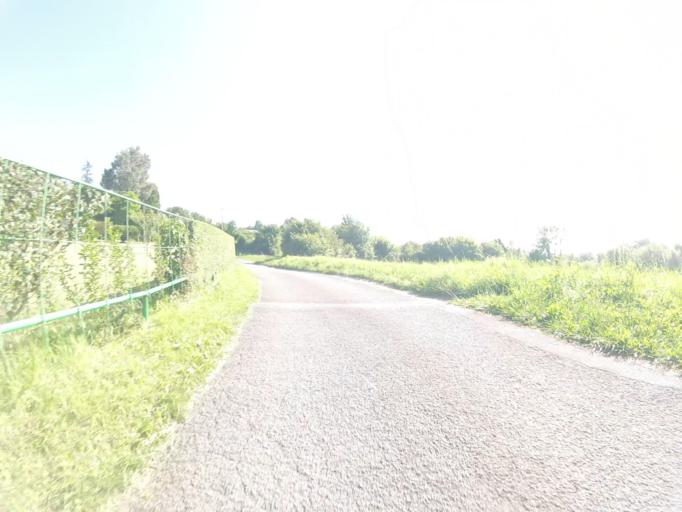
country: ES
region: Basque Country
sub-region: Provincia de Guipuzcoa
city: Astigarraga
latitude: 43.2773
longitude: -1.9357
